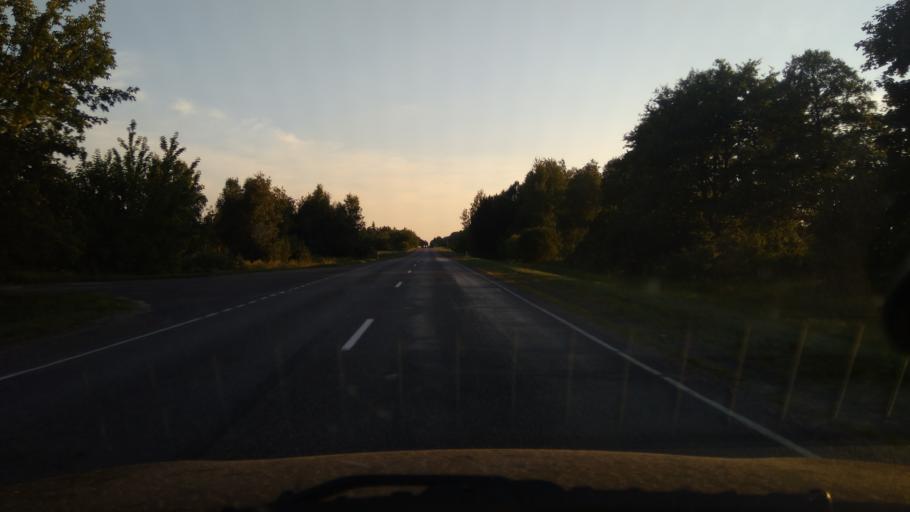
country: BY
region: Brest
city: Nyakhachava
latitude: 52.6182
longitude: 25.1535
